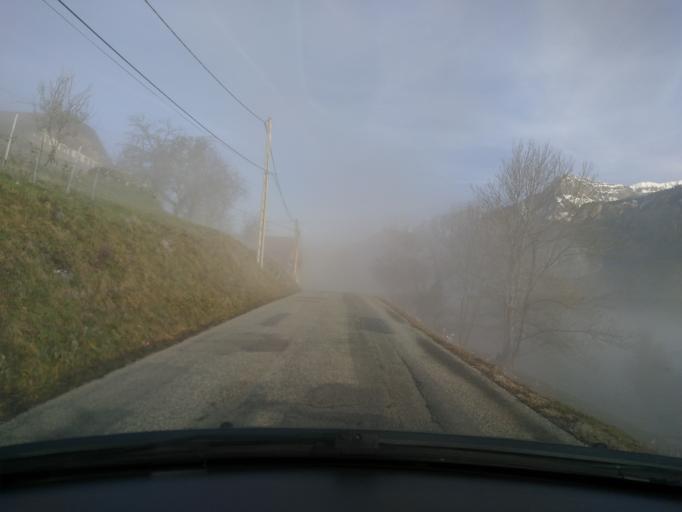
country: FR
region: Rhone-Alpes
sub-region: Departement de la Haute-Savoie
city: Sallanches
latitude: 45.9458
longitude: 6.6204
